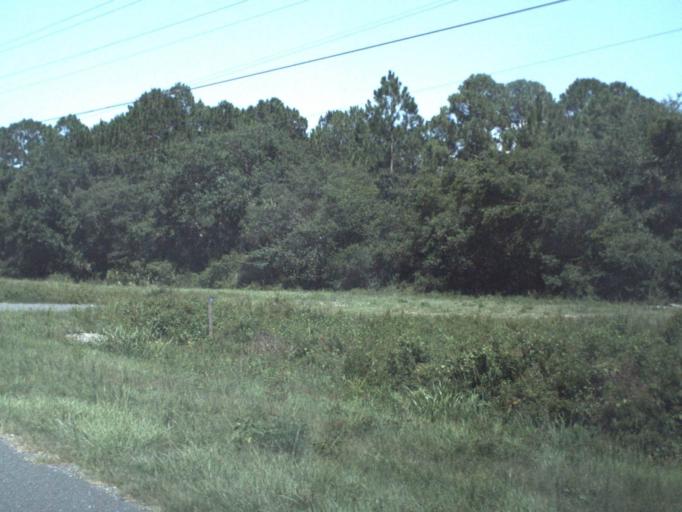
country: US
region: Florida
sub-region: Levy County
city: Chiefland
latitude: 29.1816
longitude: -83.0191
